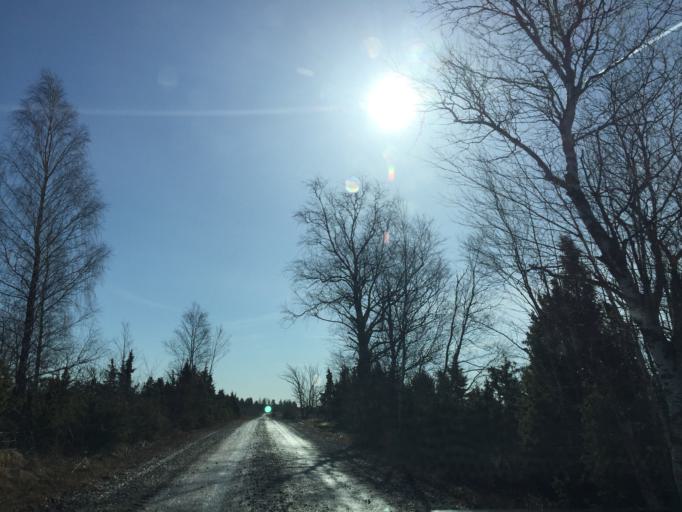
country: EE
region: Laeaene
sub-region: Haapsalu linn
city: Haapsalu
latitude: 58.6821
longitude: 23.5297
